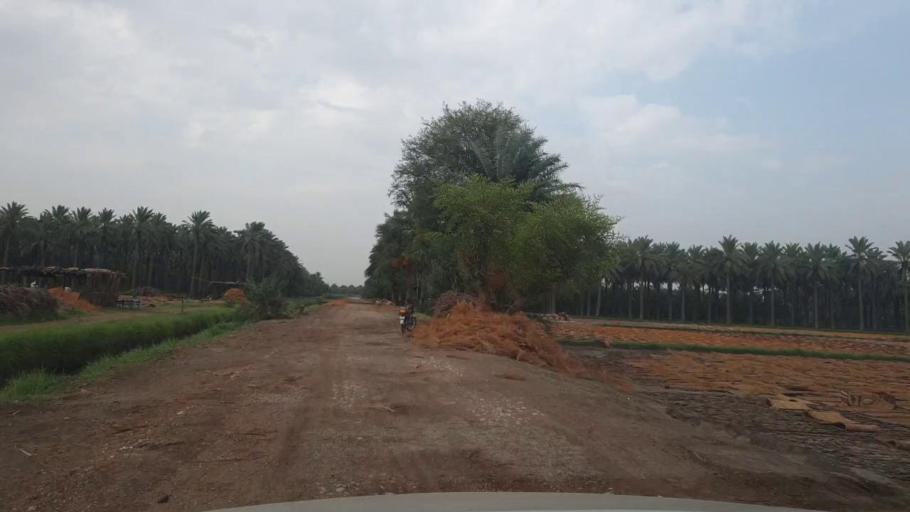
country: PK
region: Sindh
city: Sukkur
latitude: 27.6118
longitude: 68.8358
